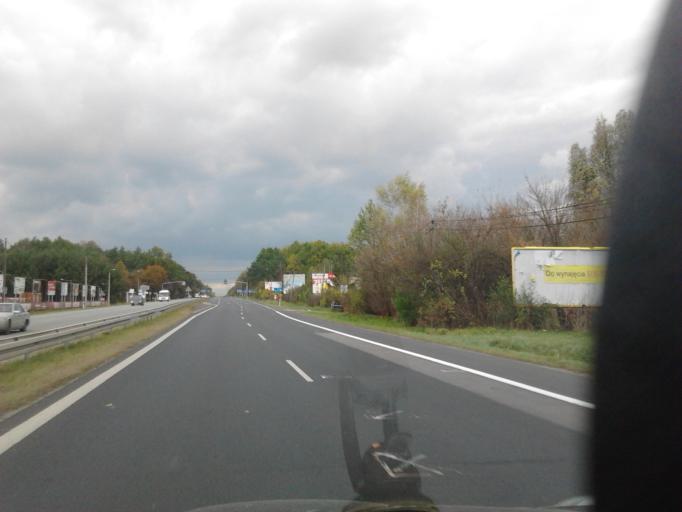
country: PL
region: Masovian Voivodeship
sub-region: Powiat piaseczynski
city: Lesznowola
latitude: 52.0900
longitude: 20.8814
